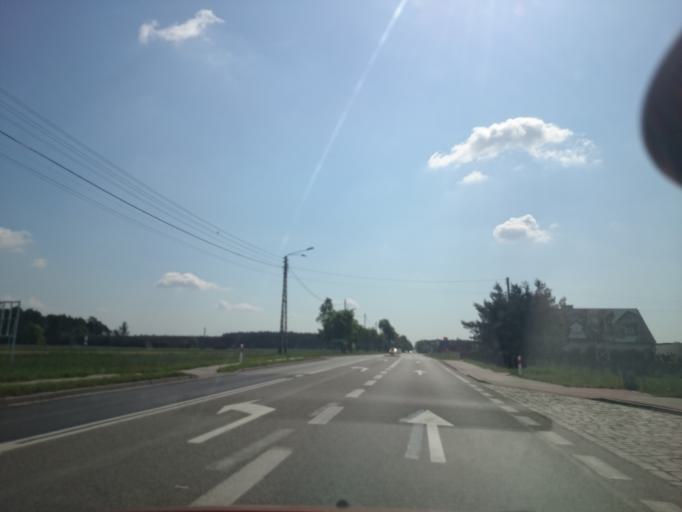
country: PL
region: Opole Voivodeship
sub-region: Powiat opolski
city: Naklo
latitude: 50.5775
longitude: 18.1282
